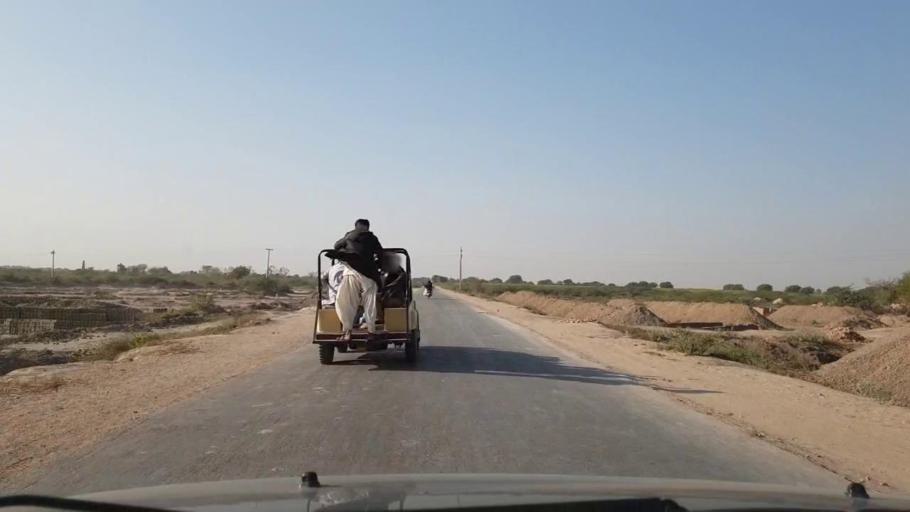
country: PK
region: Sindh
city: Tando Ghulam Ali
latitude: 25.1432
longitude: 68.8692
